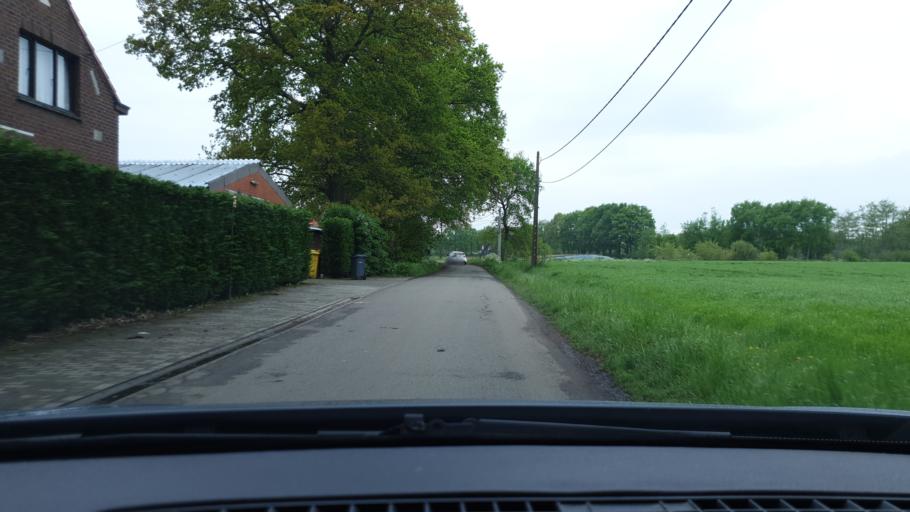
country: BE
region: Flanders
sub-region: Provincie Antwerpen
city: Meerhout
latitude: 51.1212
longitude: 5.0358
